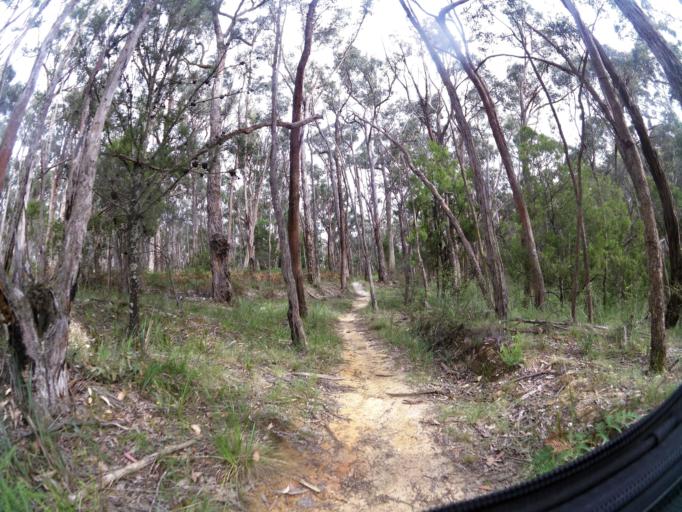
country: AU
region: Victoria
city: Brown Hill
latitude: -37.4694
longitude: 143.9096
